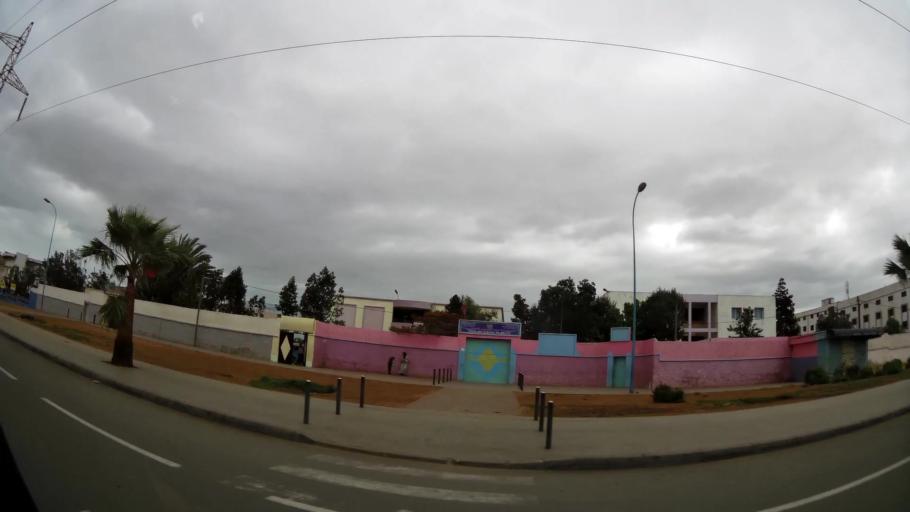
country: MA
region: Grand Casablanca
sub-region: Mediouna
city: Tit Mellil
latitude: 33.5659
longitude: -7.5297
